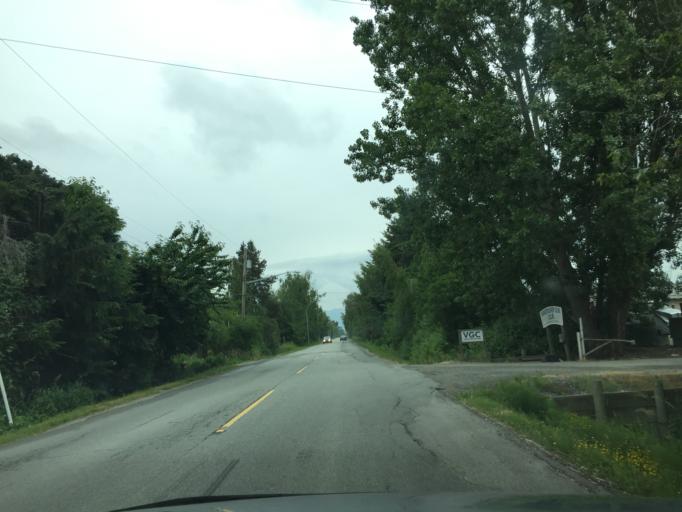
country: CA
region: British Columbia
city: Richmond
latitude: 49.1589
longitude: -123.0806
